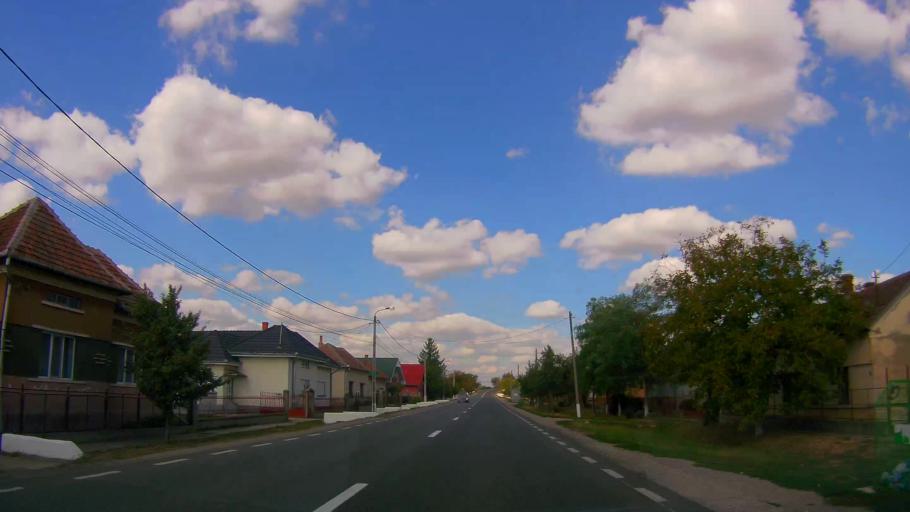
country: RO
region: Satu Mare
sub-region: Comuna Beltiug
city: Beltiug
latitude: 47.5529
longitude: 22.8458
